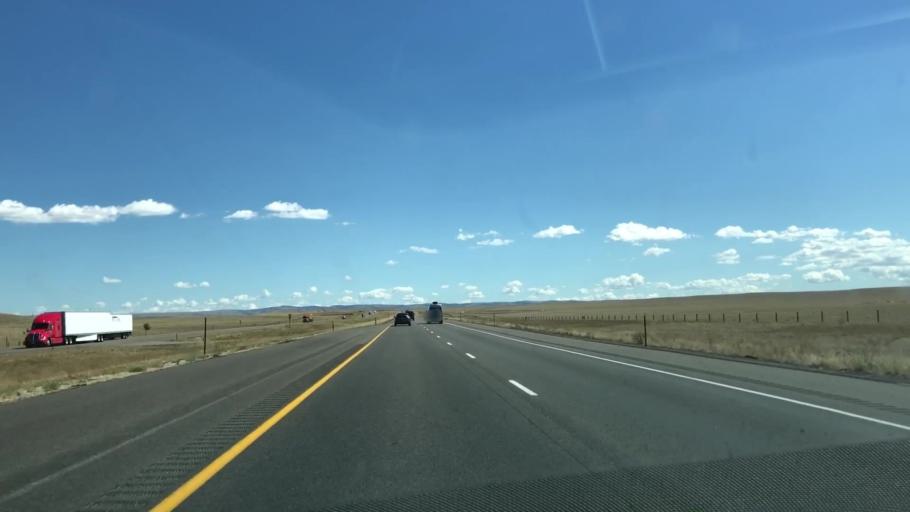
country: US
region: Wyoming
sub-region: Albany County
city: Laramie
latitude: 41.3593
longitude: -105.7619
